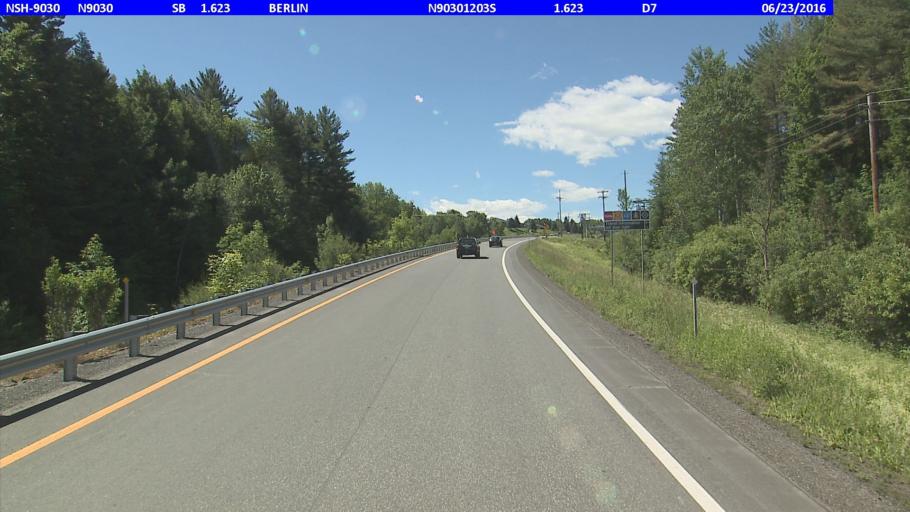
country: US
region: Vermont
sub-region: Washington County
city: Montpelier
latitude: 44.2234
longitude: -72.5578
